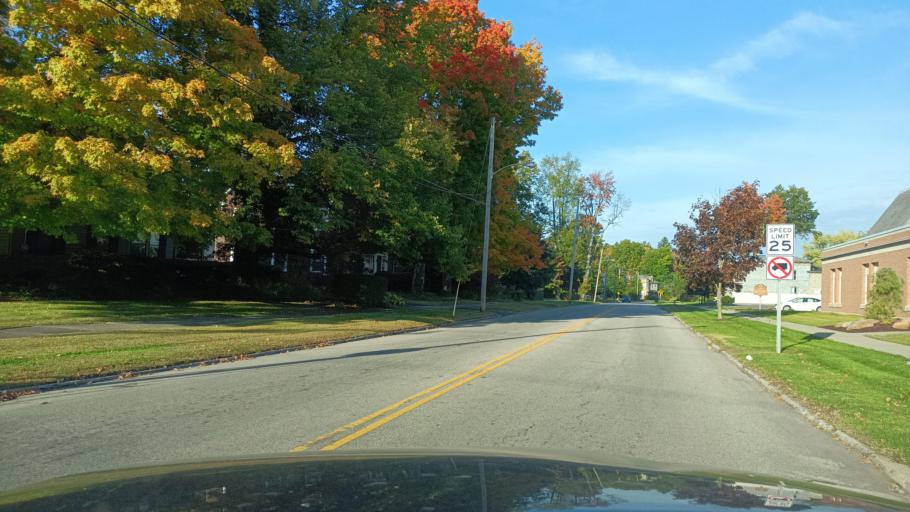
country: CN
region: Xinjiang Uygur Zizhiqu
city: Jiamu
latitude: 41.2403
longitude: 80.8236
